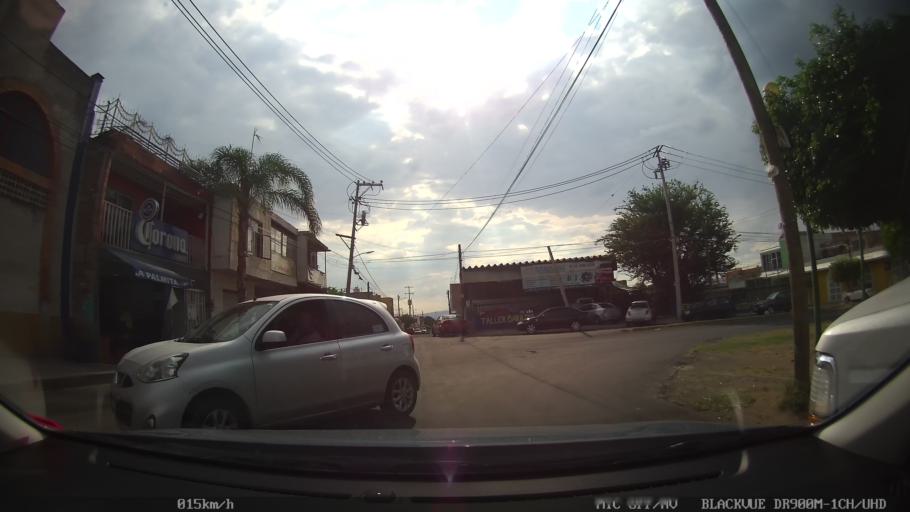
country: MX
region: Jalisco
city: Tonala
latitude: 20.6209
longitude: -103.2587
